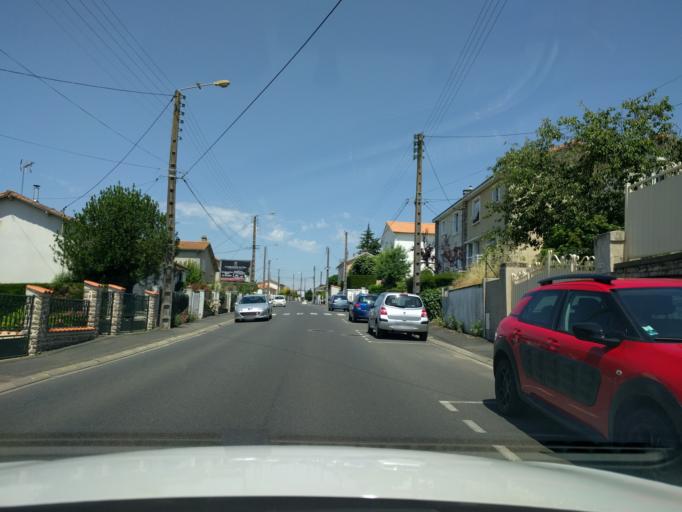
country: FR
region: Poitou-Charentes
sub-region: Departement des Deux-Sevres
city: Niort
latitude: 46.3451
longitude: -0.4762
